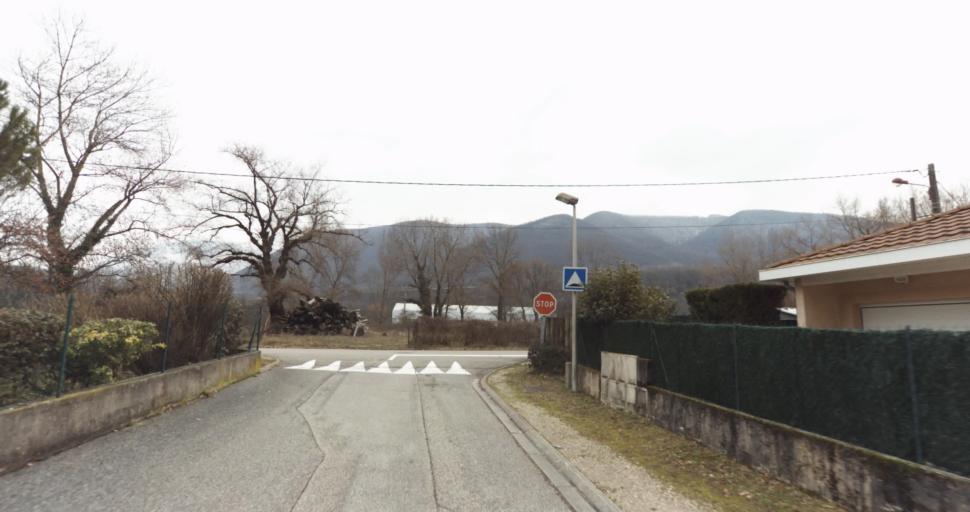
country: FR
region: Rhone-Alpes
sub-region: Departement de l'Isere
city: Vif
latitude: 45.0410
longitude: 5.6567
